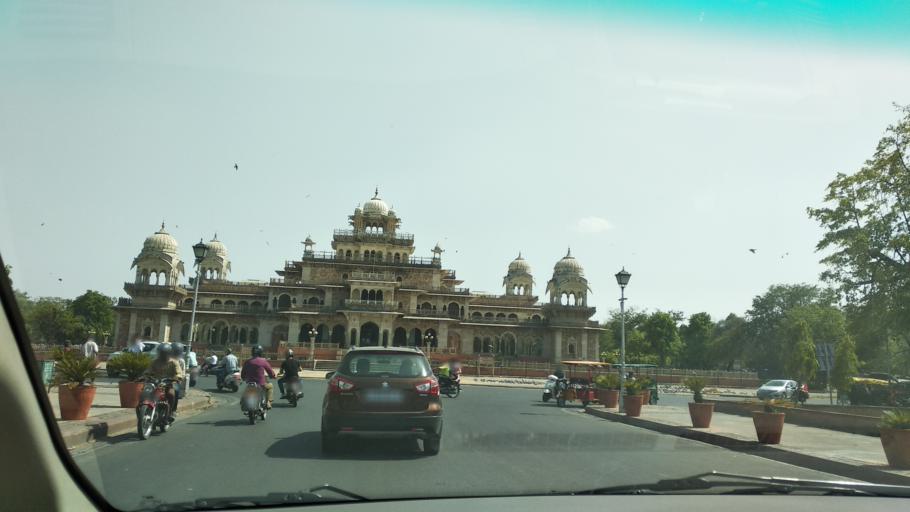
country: IN
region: Rajasthan
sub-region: Jaipur
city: Jaipur
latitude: 26.9128
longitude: 75.8198
